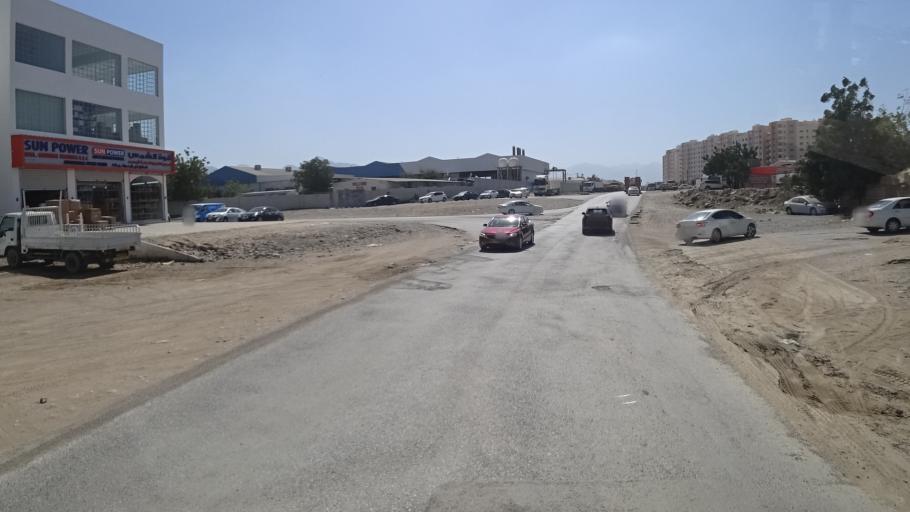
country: OM
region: Muhafazat Masqat
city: Bawshar
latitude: 23.5786
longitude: 58.3688
